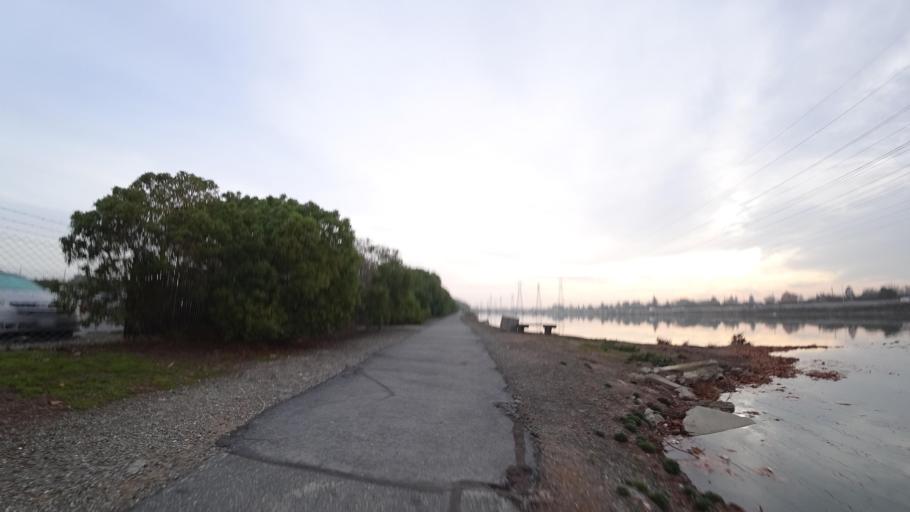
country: US
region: California
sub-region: San Mateo County
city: Burlingame
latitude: 37.5887
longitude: -122.3459
